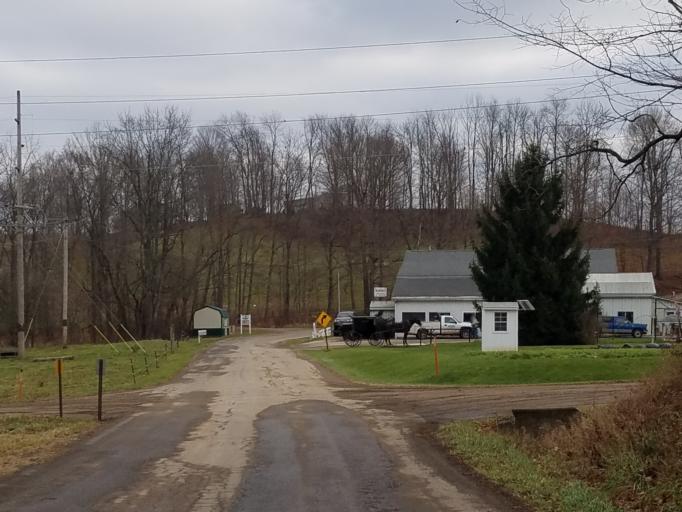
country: US
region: Ohio
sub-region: Knox County
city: Danville
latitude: 40.5435
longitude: -82.3349
